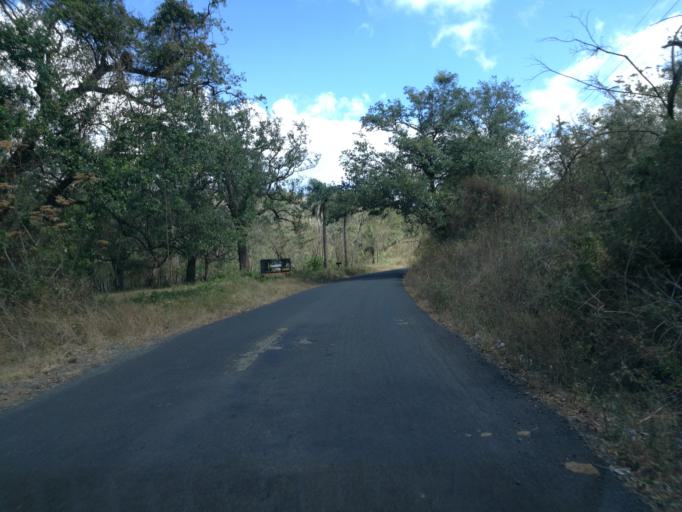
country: CR
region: Guanacaste
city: Liberia
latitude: 10.7366
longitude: -85.3870
